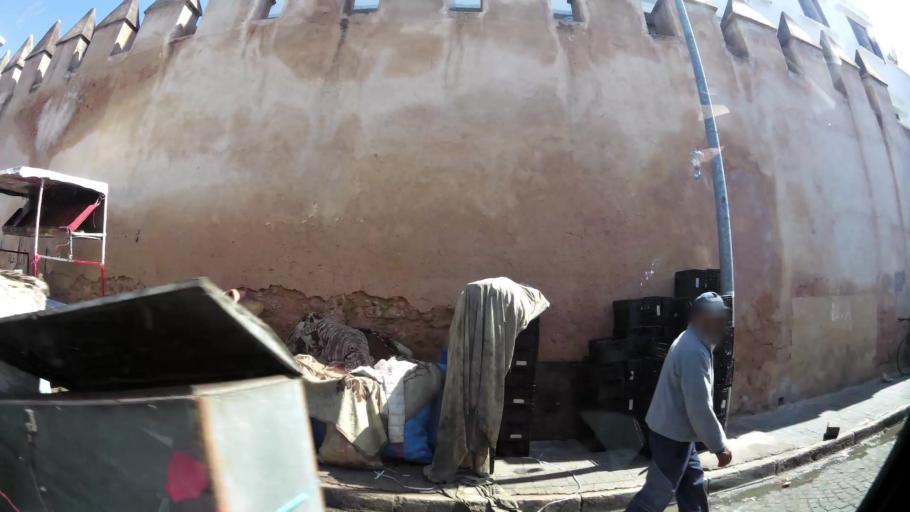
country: MA
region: Grand Casablanca
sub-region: Casablanca
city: Casablanca
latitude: 33.5978
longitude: -7.6213
